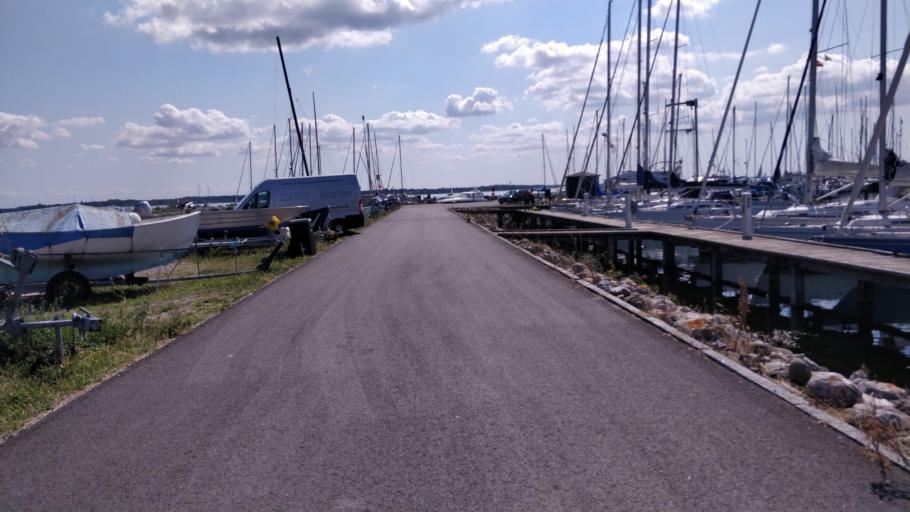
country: DK
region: Capital Region
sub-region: Halsnaes Kommune
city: Hundested
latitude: 55.9438
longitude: 11.8676
